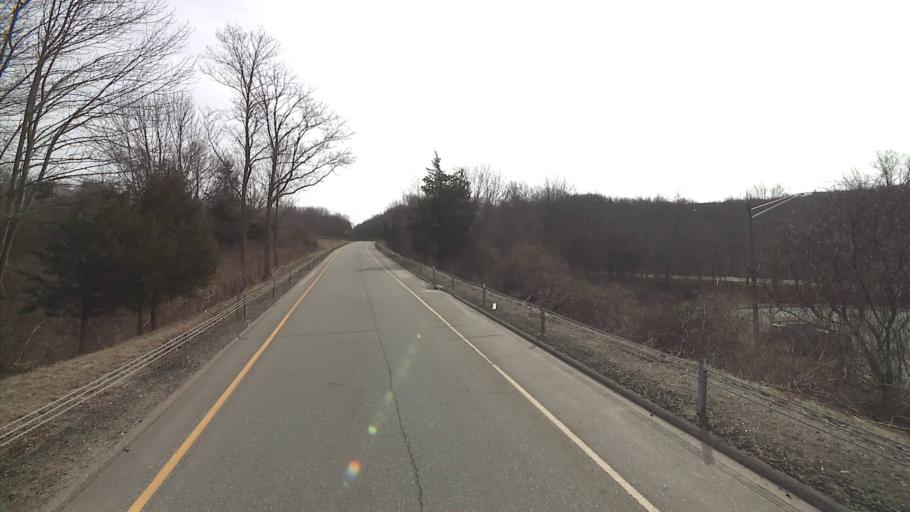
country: US
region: Connecticut
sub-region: Middlesex County
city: Chester Center
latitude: 41.3991
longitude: -72.4735
